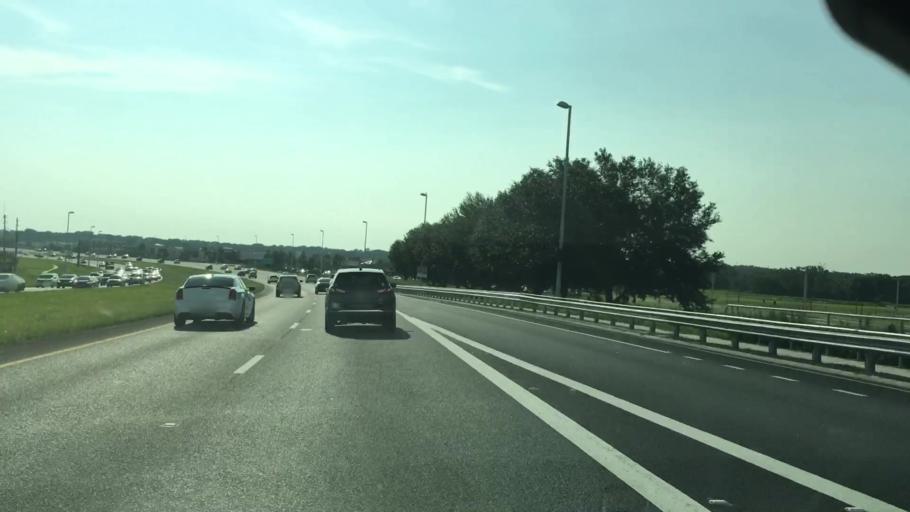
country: US
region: Florida
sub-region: Hillsborough County
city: Pebble Creek
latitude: 28.1955
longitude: -82.3865
